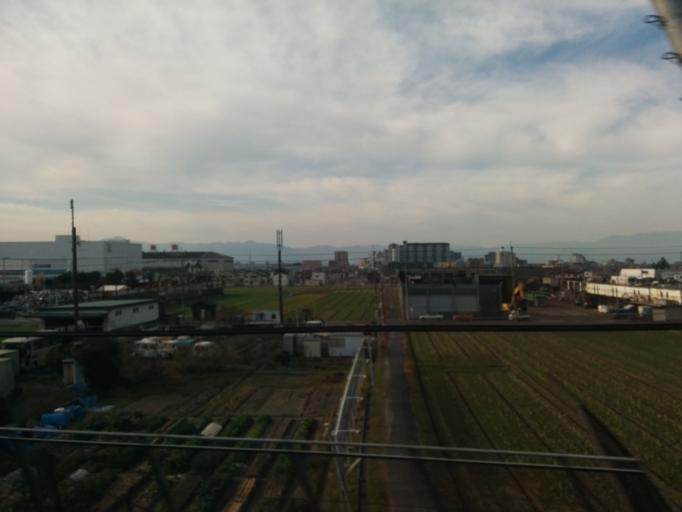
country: JP
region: Shiga Prefecture
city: Moriyama
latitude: 35.0454
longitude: 136.0059
